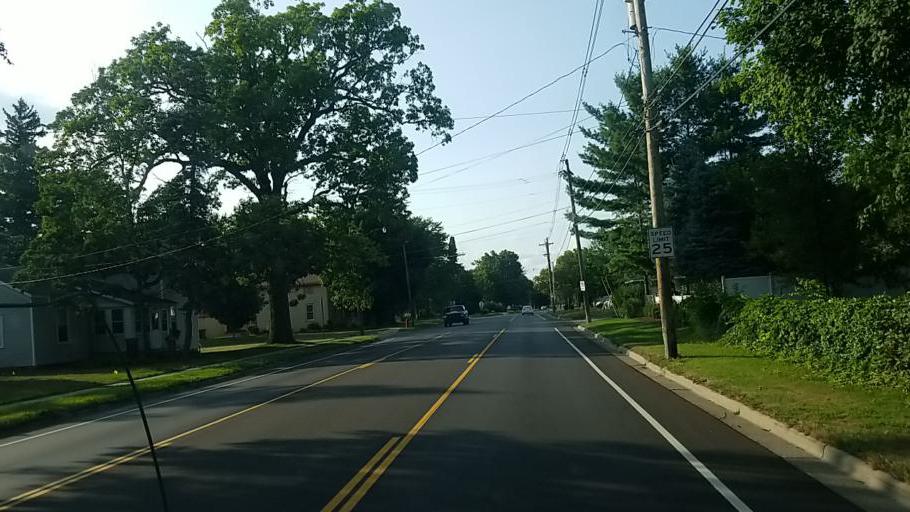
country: US
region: Michigan
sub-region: Kent County
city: Lowell
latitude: 42.9390
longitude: -85.3439
